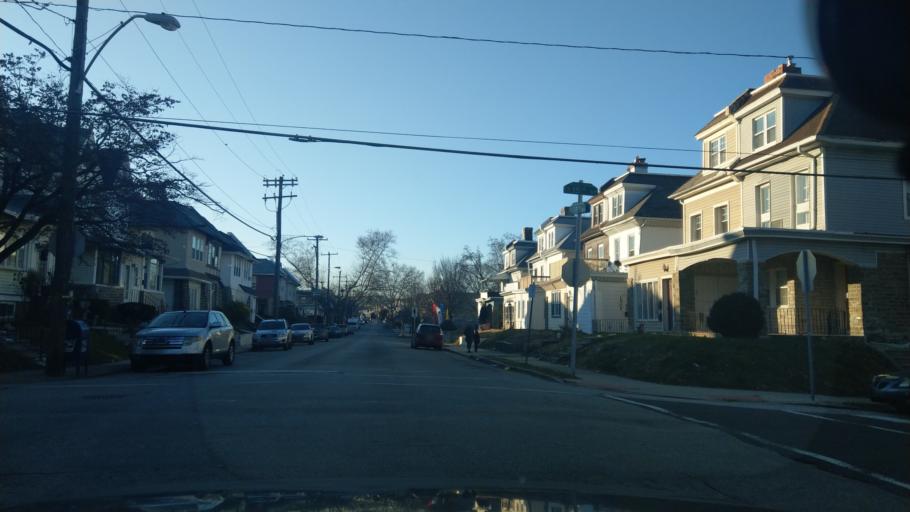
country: US
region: Pennsylvania
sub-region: Montgomery County
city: Wyncote
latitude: 40.0569
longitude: -75.1424
